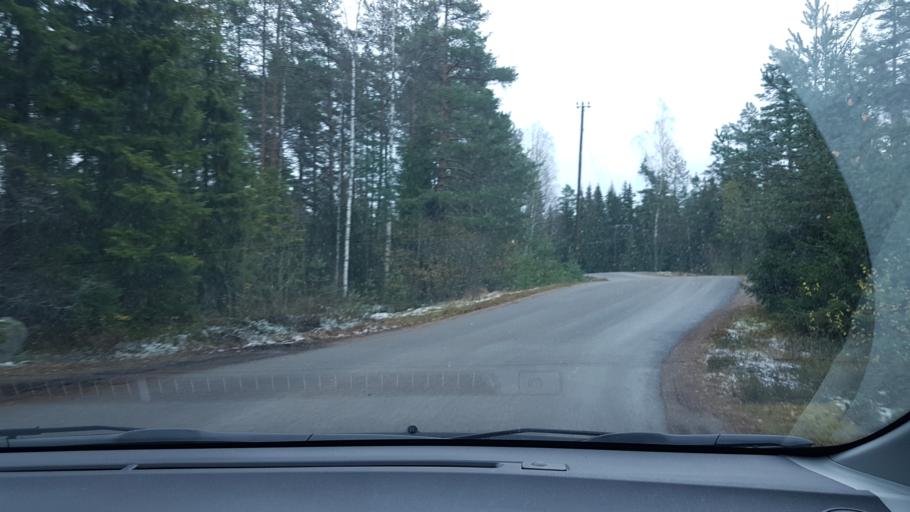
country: FI
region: Uusimaa
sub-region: Helsinki
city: Vantaa
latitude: 60.2839
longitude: 25.1602
